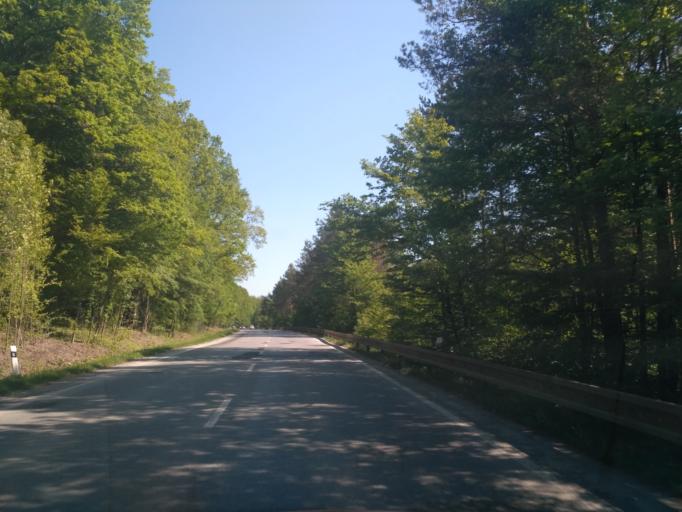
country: SK
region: Presovsky
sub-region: Okres Presov
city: Presov
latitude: 48.9735
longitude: 21.1701
